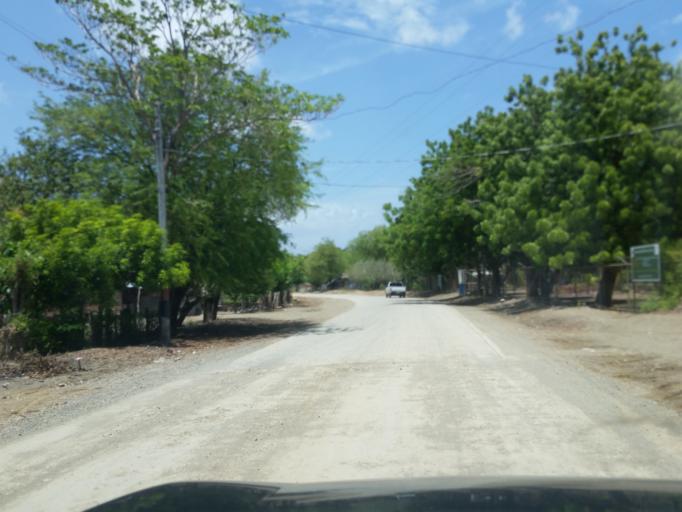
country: NI
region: Rivas
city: Tola
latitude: 11.4608
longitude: -86.0803
